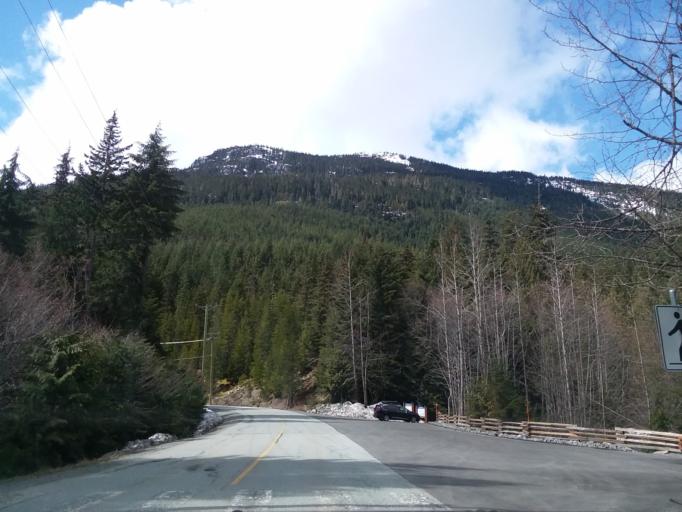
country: CA
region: British Columbia
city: Whistler
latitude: 50.1302
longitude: -122.9847
